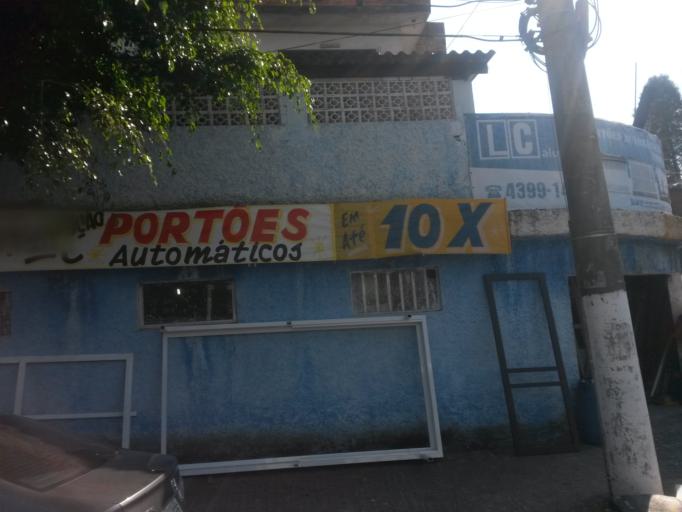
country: BR
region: Sao Paulo
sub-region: Sao Bernardo Do Campo
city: Sao Bernardo do Campo
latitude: -23.7009
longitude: -46.5673
